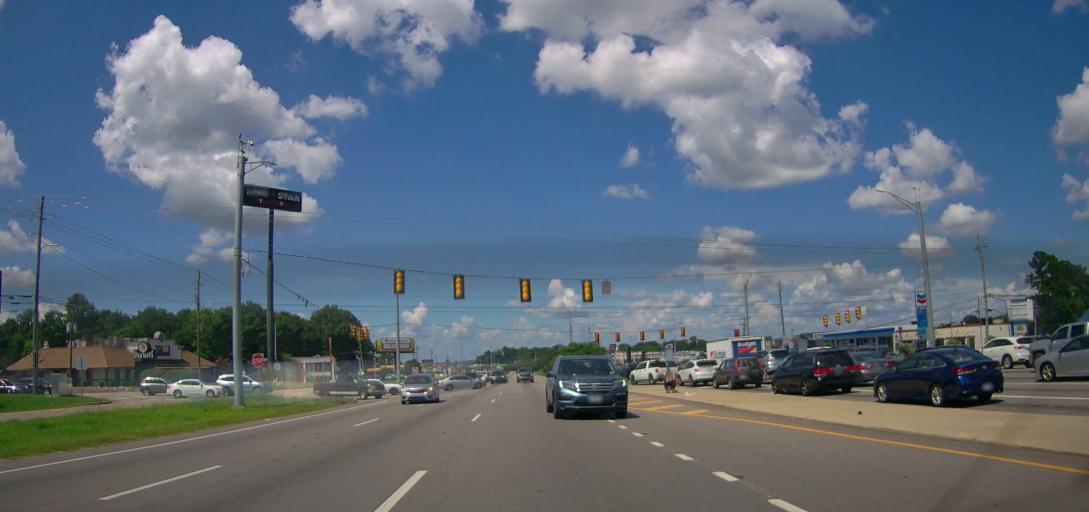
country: US
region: Alabama
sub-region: Montgomery County
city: Montgomery
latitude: 32.3652
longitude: -86.2124
